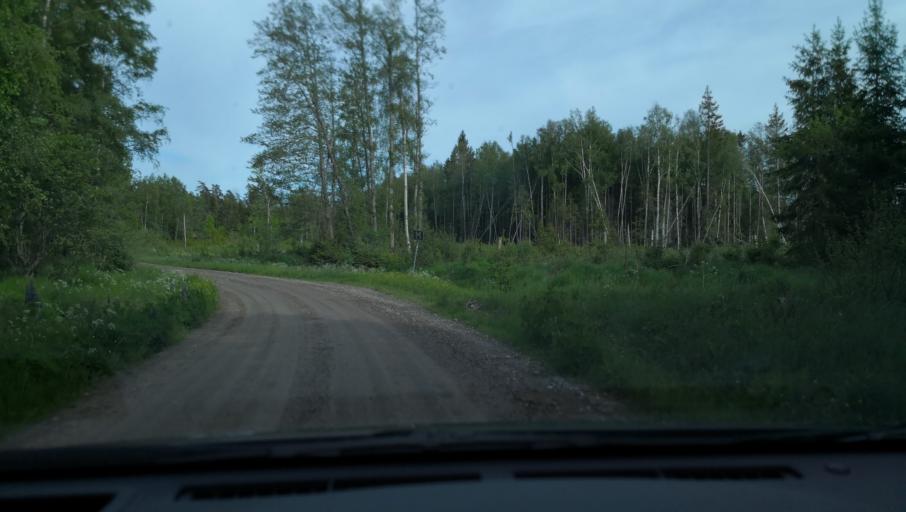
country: SE
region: Vaestmanland
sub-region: Arboga Kommun
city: Tyringe
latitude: 59.3645
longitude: 15.9892
